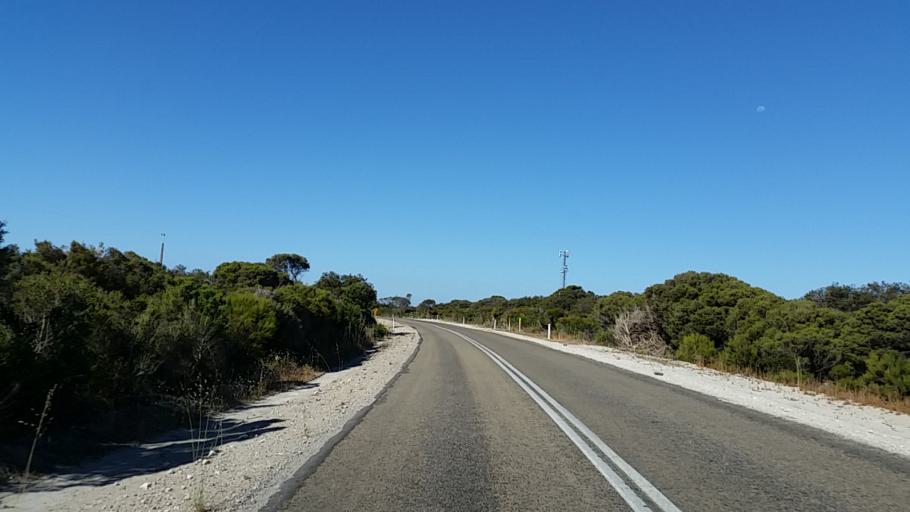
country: AU
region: South Australia
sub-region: Yorke Peninsula
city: Honiton
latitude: -35.2460
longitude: 136.9721
